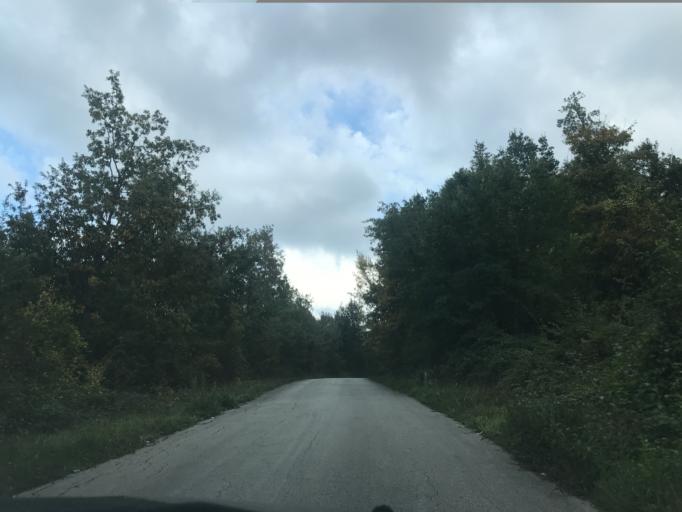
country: IT
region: Molise
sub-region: Provincia di Campobasso
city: Duronia
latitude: 41.6647
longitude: 14.4591
